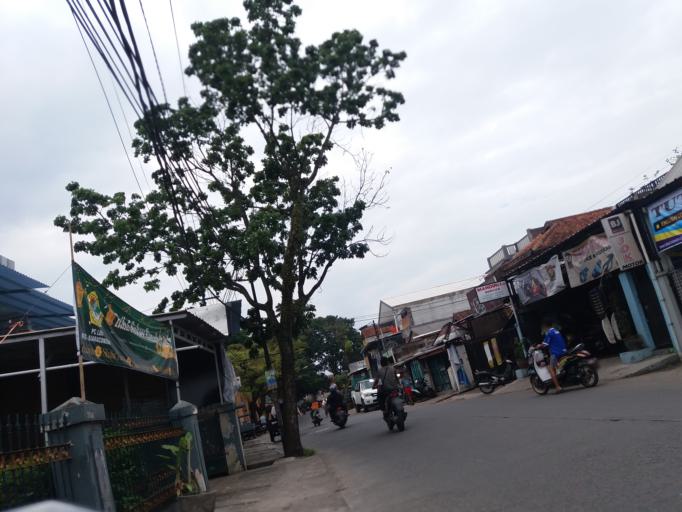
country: ID
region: West Java
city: Bandung
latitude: -6.9244
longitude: 107.6536
